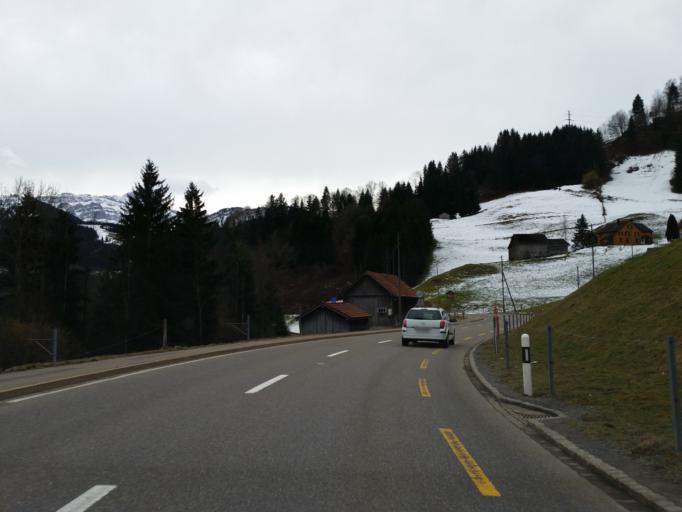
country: CH
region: Appenzell Ausserrhoden
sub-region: Bezirk Hinterland
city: Urnasch
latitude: 47.3339
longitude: 9.2898
